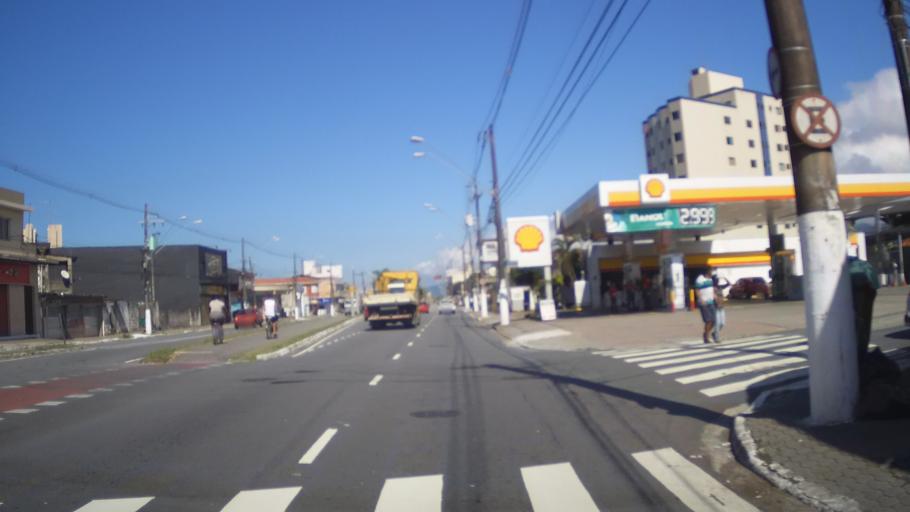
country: BR
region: Sao Paulo
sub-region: Praia Grande
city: Praia Grande
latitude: -24.0266
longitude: -46.4816
